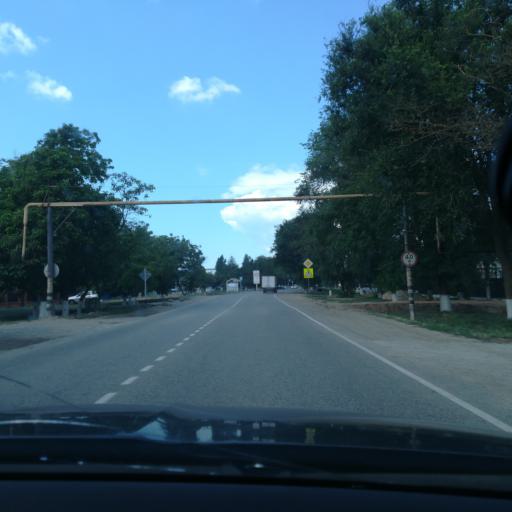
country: RU
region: Krasnodarskiy
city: Taman'
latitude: 45.2179
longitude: 36.7417
